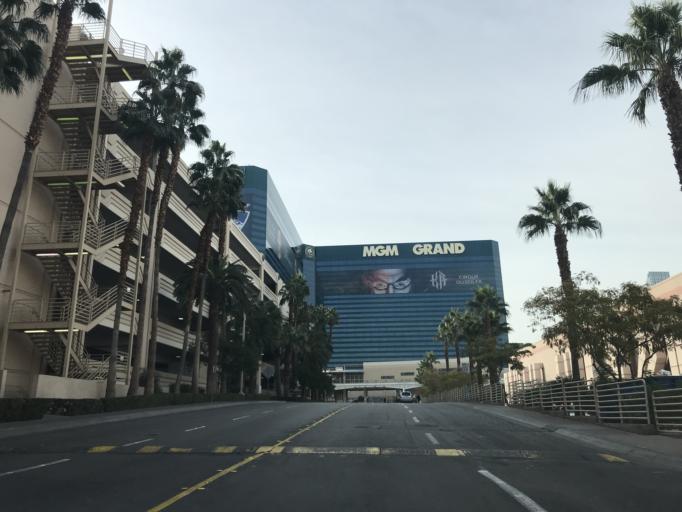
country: US
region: Nevada
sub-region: Clark County
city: Paradise
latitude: 36.1029
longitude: -115.1659
